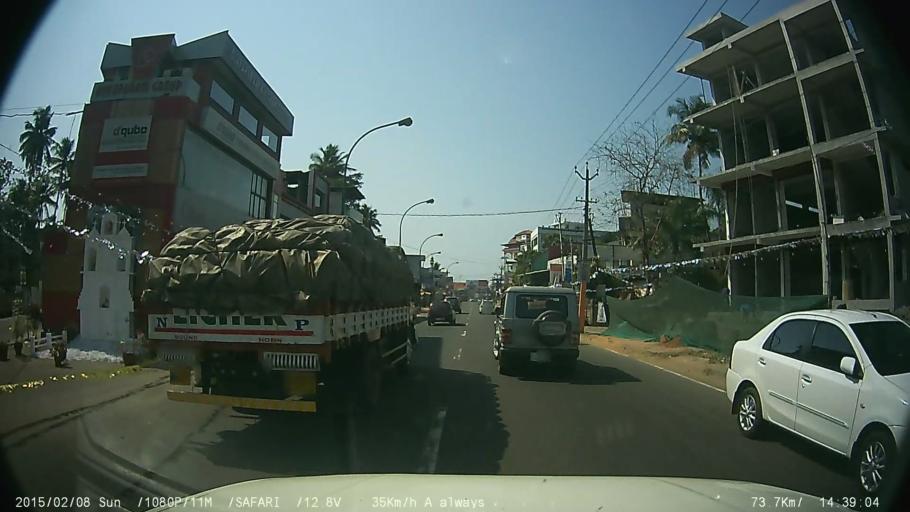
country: IN
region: Kerala
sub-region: Ernakulam
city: Angamali
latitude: 10.1886
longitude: 76.3928
